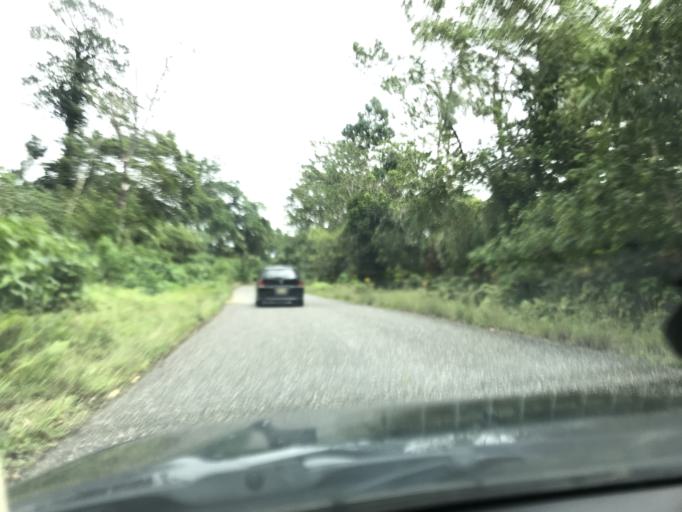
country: SB
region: Western Province
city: Gizo
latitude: -8.2317
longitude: 157.2104
